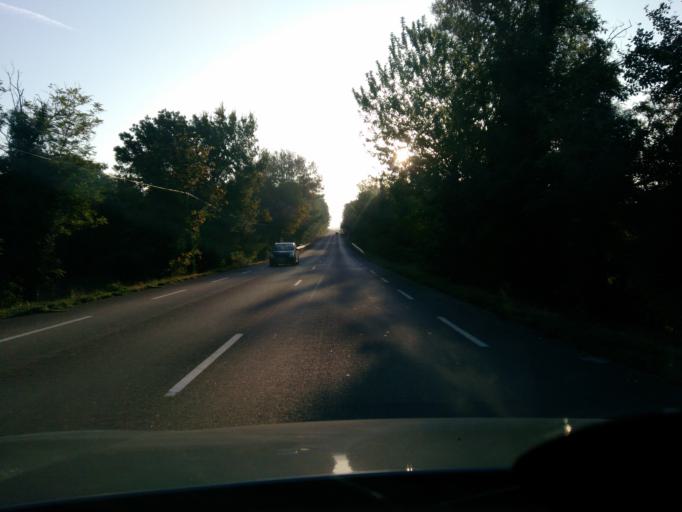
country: FR
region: Rhone-Alpes
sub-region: Departement de la Drome
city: La Garde-Adhemar
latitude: 44.4202
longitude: 4.7830
